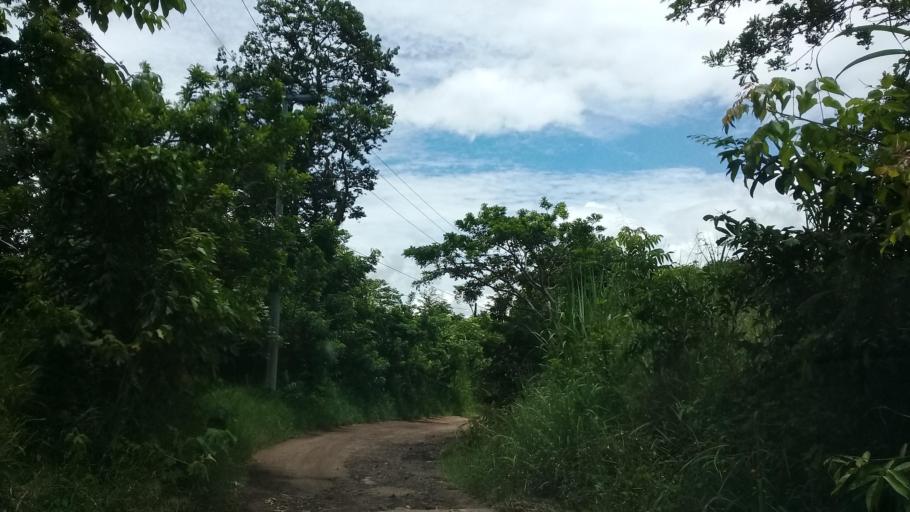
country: MX
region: Veracruz
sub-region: Naolinco
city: El Espinal
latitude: 19.5901
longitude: -96.8675
